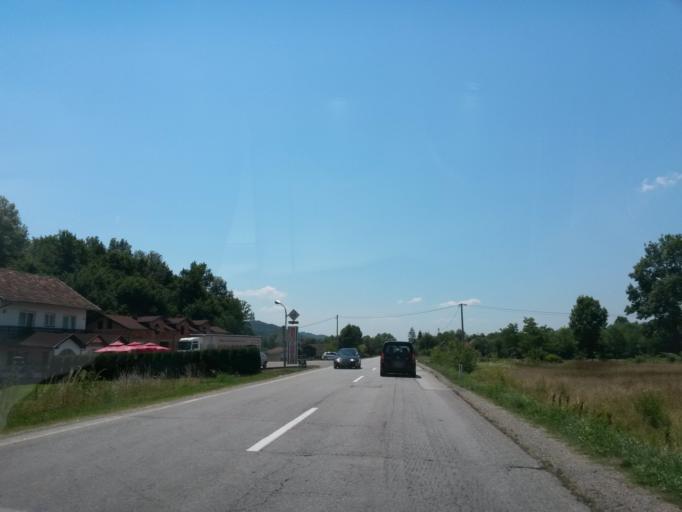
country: BA
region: Federation of Bosnia and Herzegovina
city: Lukavica
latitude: 44.9280
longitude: 18.1105
